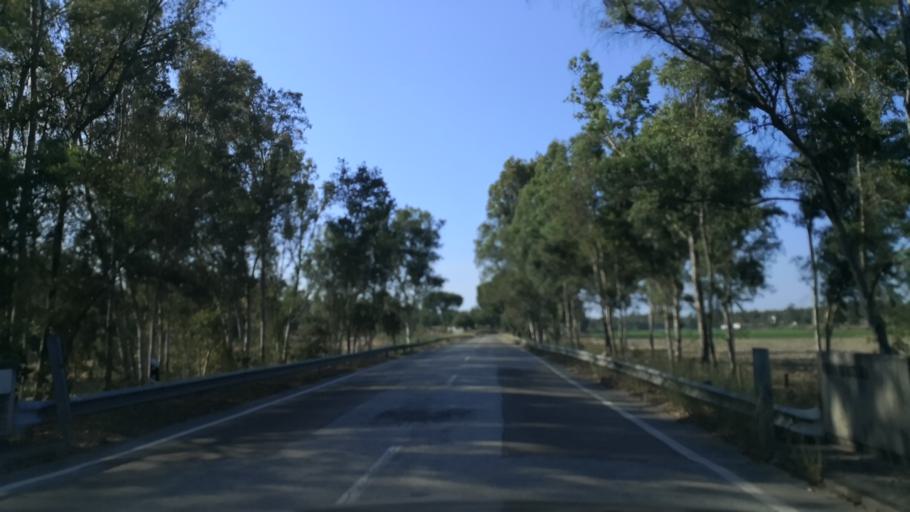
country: PT
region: Santarem
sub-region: Coruche
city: Coruche
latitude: 38.9916
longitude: -8.5537
